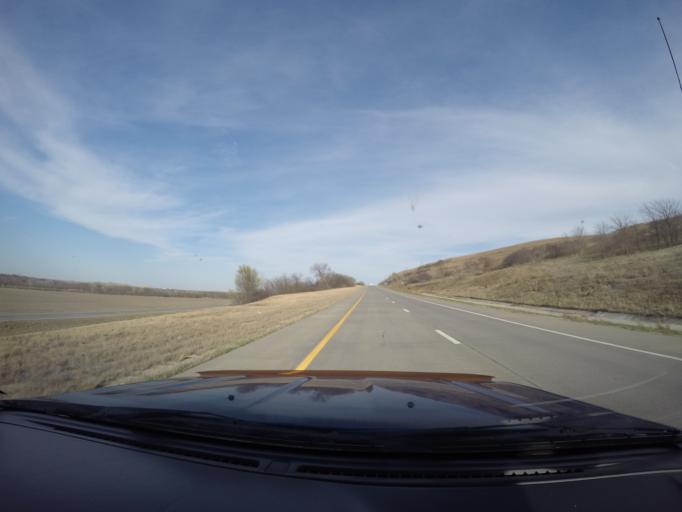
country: US
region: Kansas
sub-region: Pottawatomie County
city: Saint Marys
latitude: 39.0582
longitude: -96.1347
